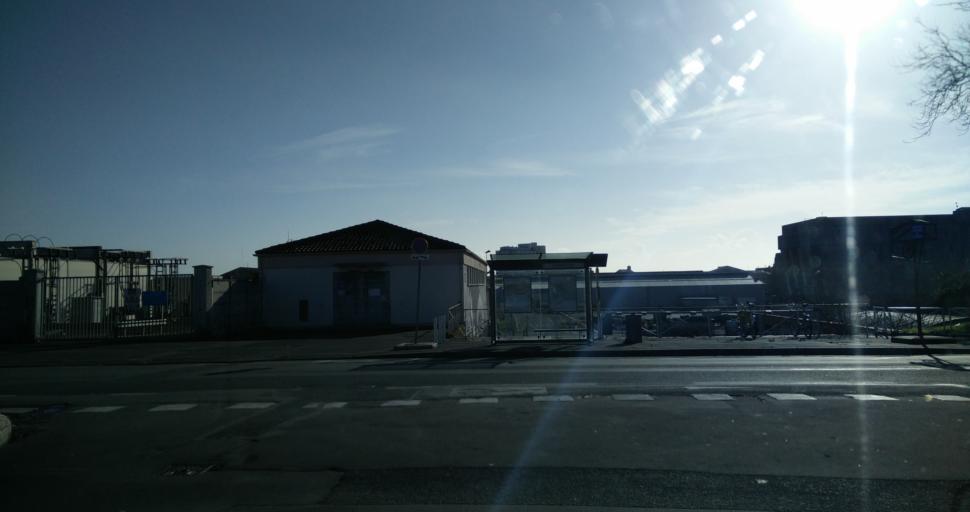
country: FR
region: Poitou-Charentes
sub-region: Departement de la Charente-Maritime
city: La Rochelle
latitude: 46.1615
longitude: -1.2073
